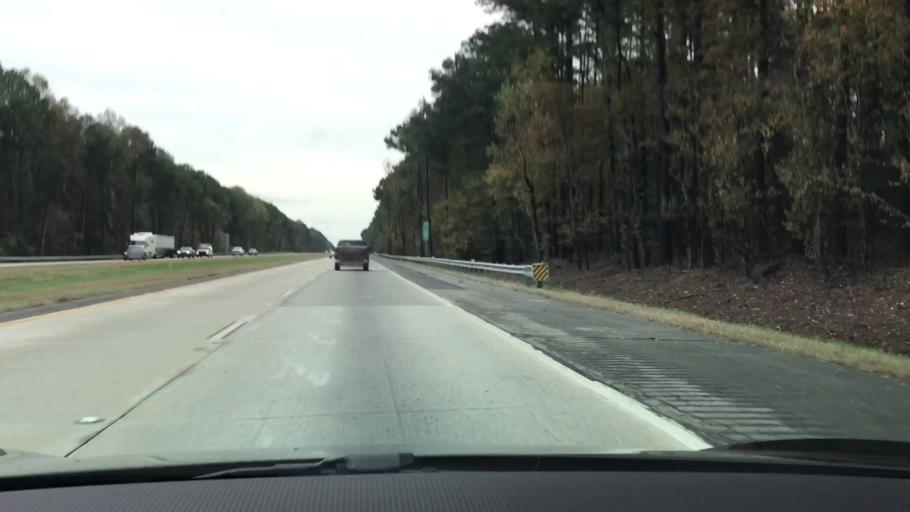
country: US
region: Georgia
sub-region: Greene County
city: Greensboro
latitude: 33.5467
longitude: -83.1857
